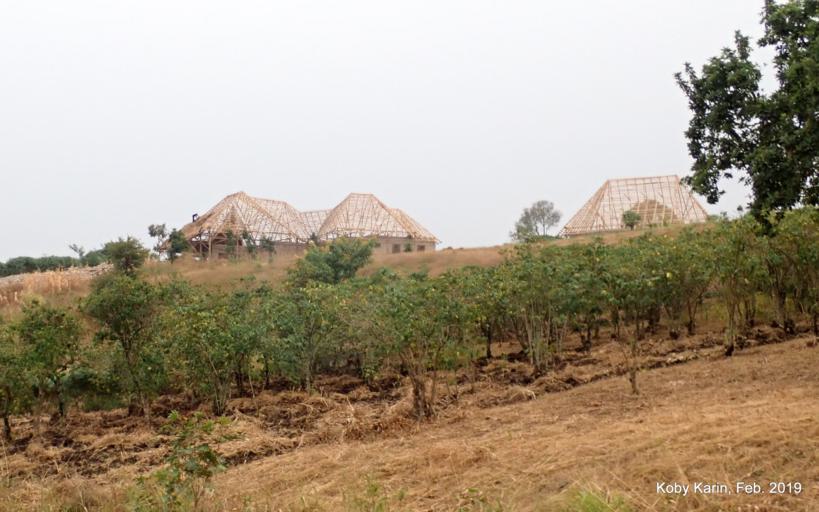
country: UG
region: Western Region
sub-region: Rubirizi District
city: Rubirizi
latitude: -0.2137
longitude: 30.0972
